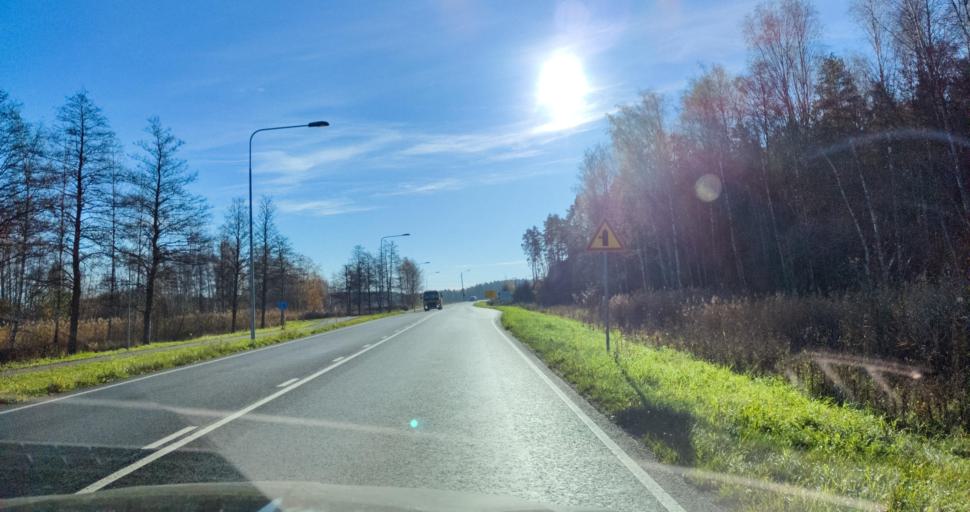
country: FI
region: Varsinais-Suomi
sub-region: Turku
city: Turku
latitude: 60.4035
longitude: 22.2410
